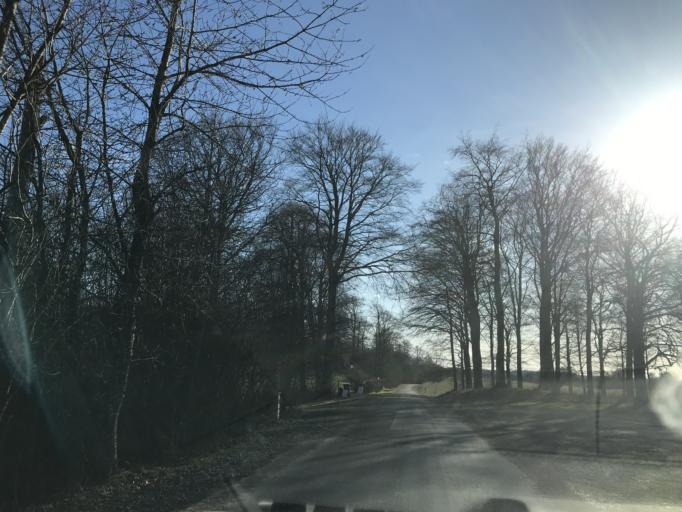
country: SE
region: Skane
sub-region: Ystads Kommun
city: Ystad
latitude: 55.5518
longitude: 13.8076
